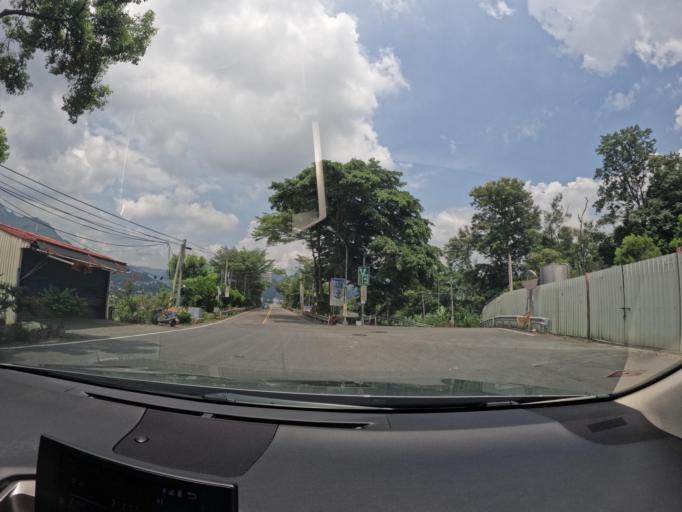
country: TW
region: Taiwan
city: Lugu
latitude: 23.8063
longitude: 120.8385
